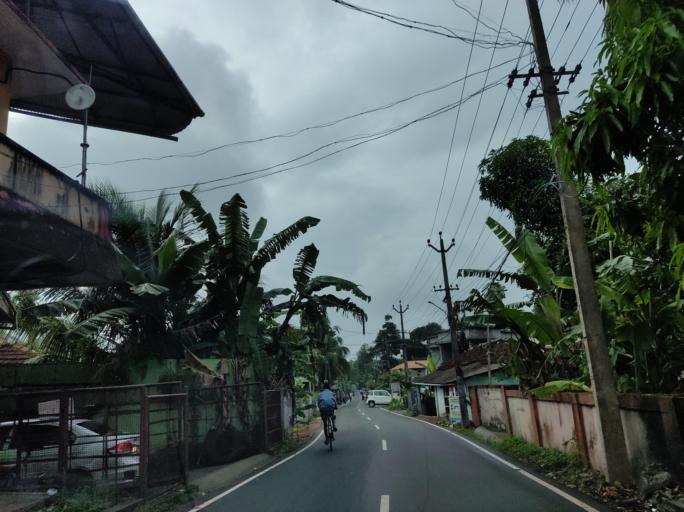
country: IN
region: Kerala
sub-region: Alappuzha
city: Mavelikara
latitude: 9.2413
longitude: 76.5533
